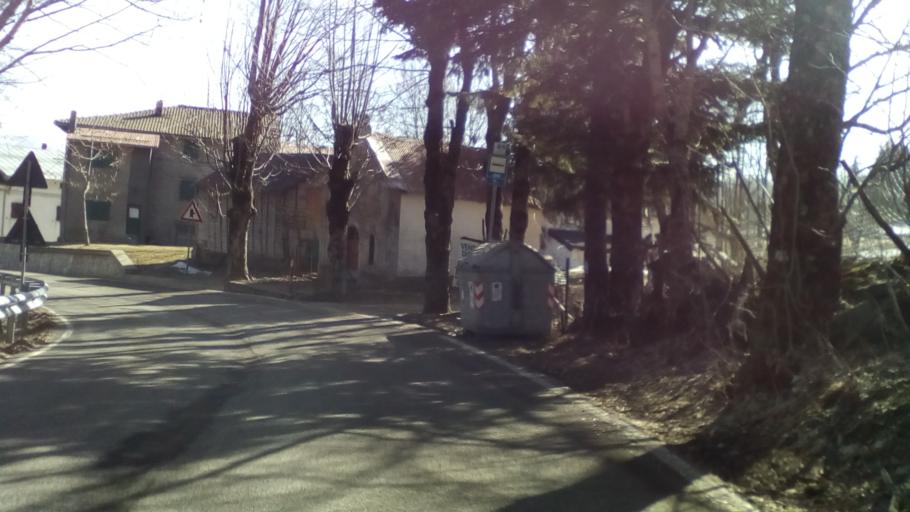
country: IT
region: Emilia-Romagna
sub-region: Provincia di Modena
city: Pievepelago
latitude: 44.1975
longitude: 10.5306
